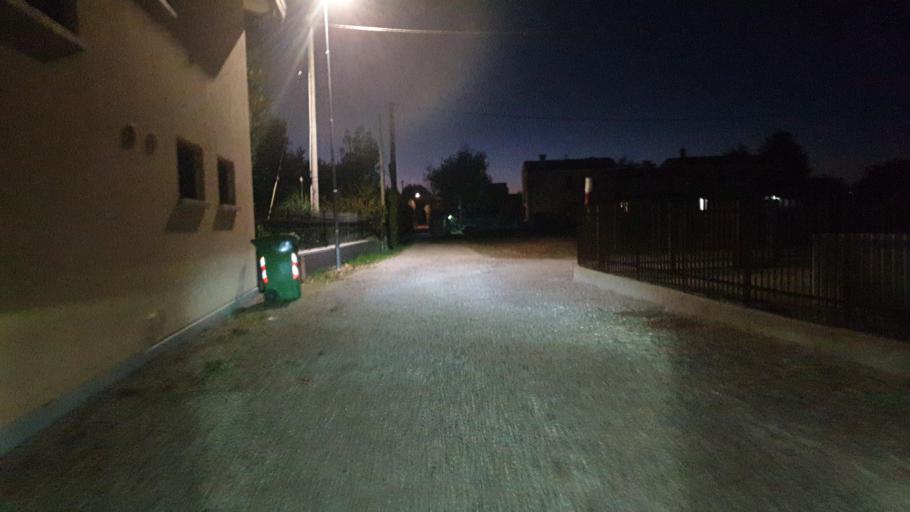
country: IT
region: Veneto
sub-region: Provincia di Padova
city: Villatora
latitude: 45.3871
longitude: 11.9725
